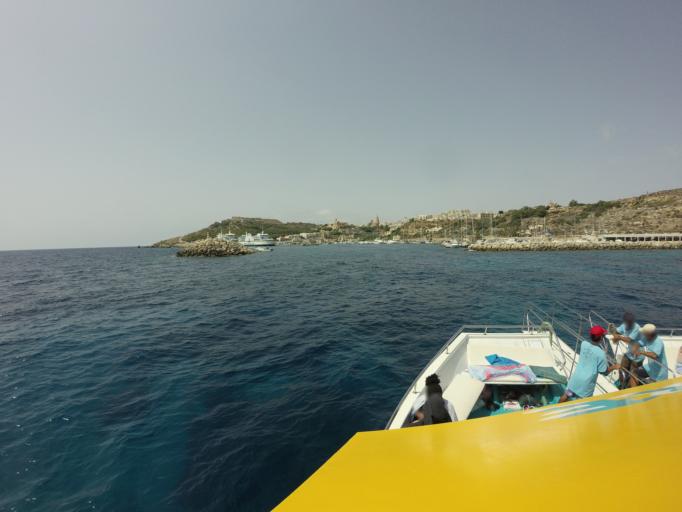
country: MT
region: Ghajnsielem
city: Mgarr
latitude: 36.0255
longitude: 14.3032
